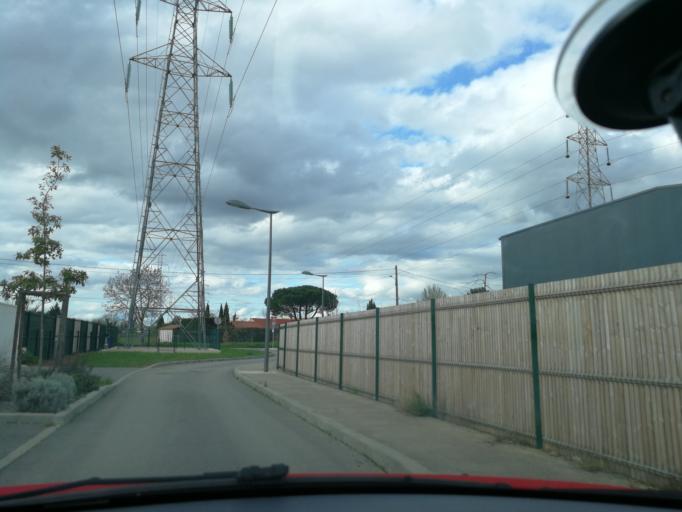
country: FR
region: Midi-Pyrenees
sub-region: Departement de la Haute-Garonne
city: Blagnac
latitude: 43.6363
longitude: 1.4158
